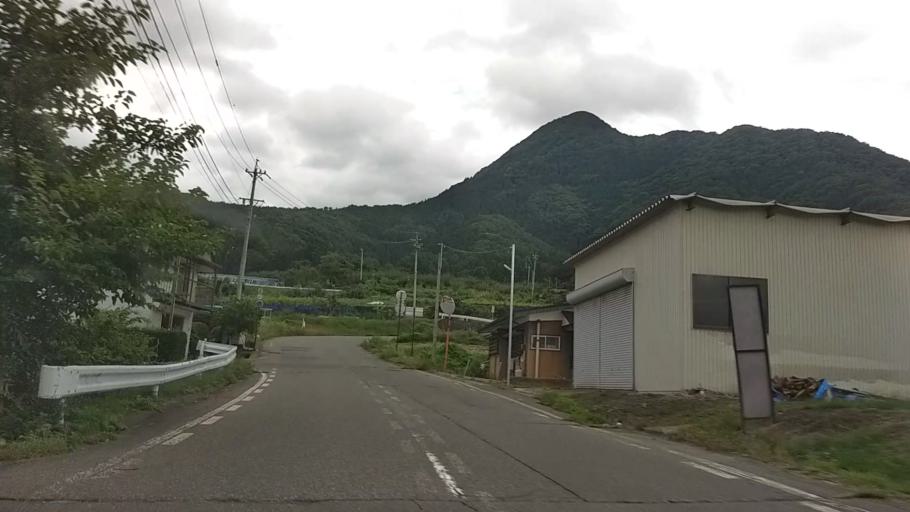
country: JP
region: Nagano
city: Iiyama
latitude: 36.8170
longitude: 138.3645
